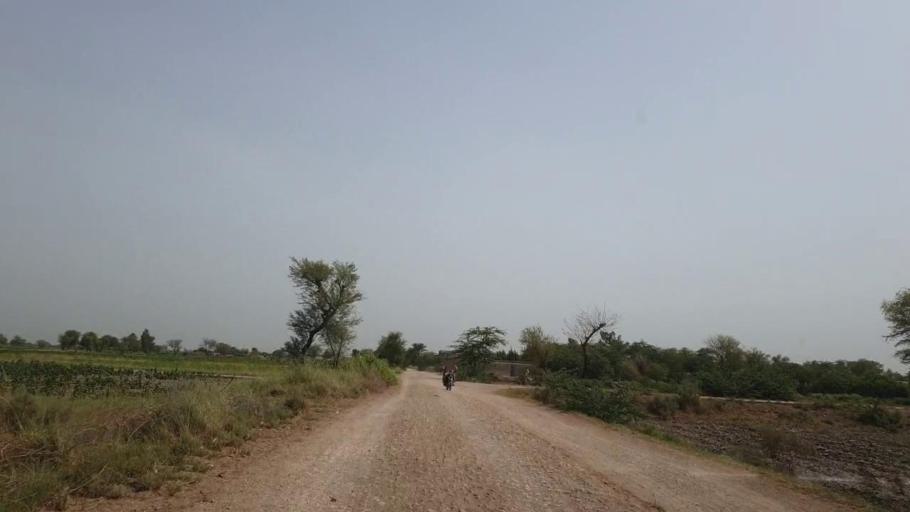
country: PK
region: Sindh
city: Sakrand
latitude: 26.1190
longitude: 68.3688
